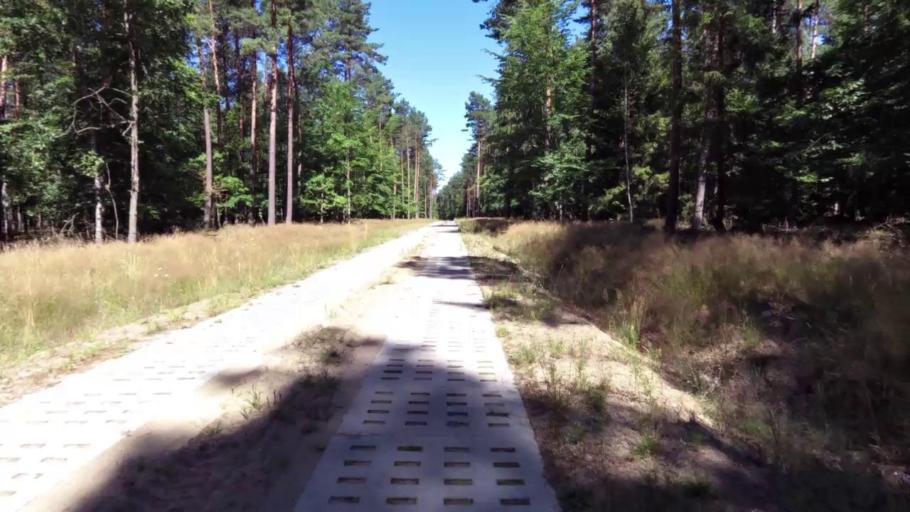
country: PL
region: West Pomeranian Voivodeship
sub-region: Powiat szczecinecki
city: Szczecinek
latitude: 53.6049
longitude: 16.6630
